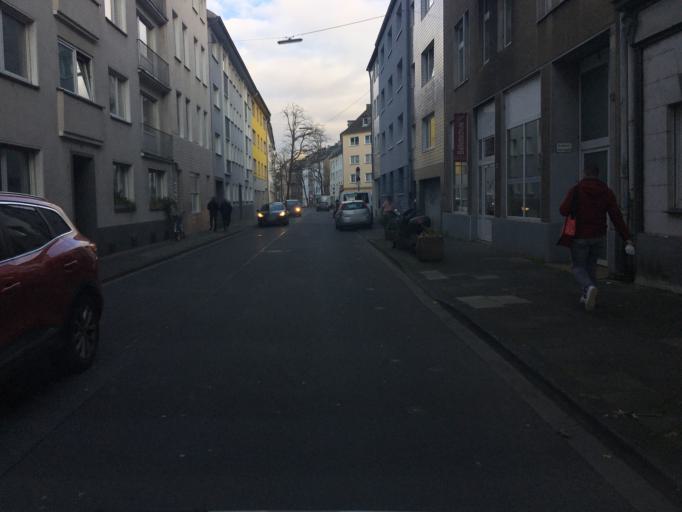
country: DE
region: North Rhine-Westphalia
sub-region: Regierungsbezirk Koln
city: Muelheim
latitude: 50.9678
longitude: 7.0035
